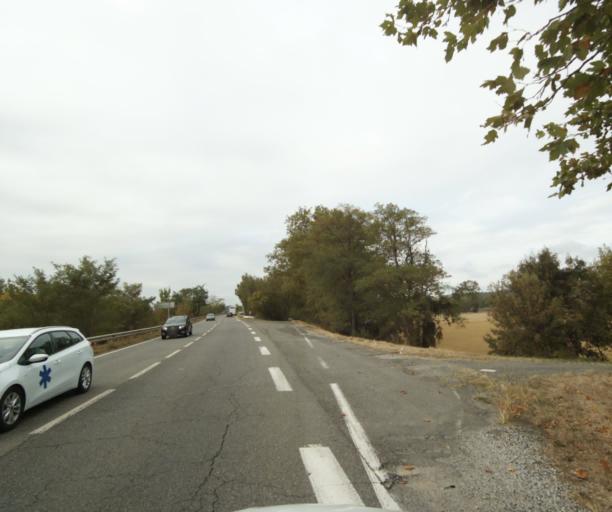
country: FR
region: Midi-Pyrenees
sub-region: Departement de la Haute-Garonne
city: Villefranche-de-Lauragais
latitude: 43.3956
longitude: 1.7010
